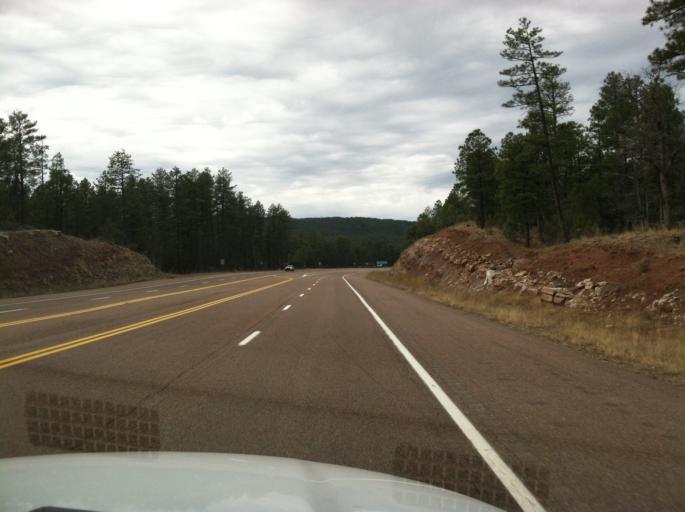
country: US
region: Arizona
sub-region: Gila County
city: Star Valley
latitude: 34.2953
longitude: -110.9691
